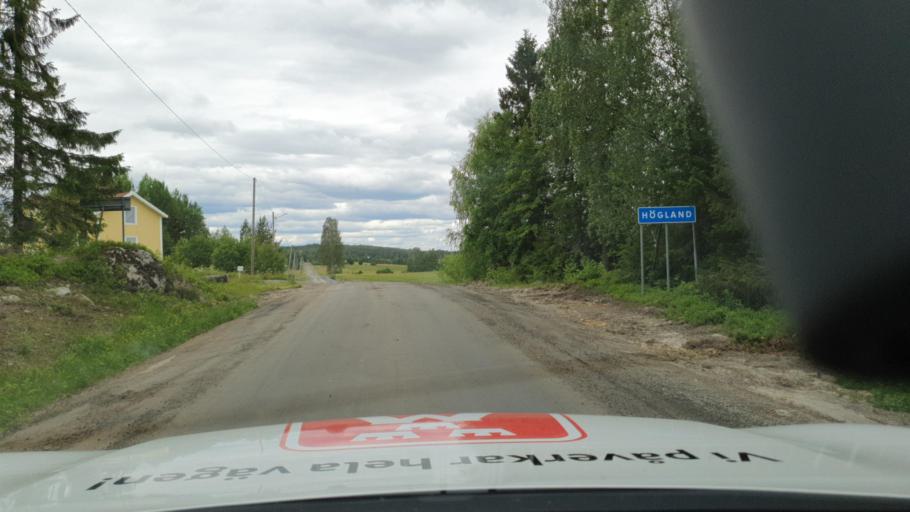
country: SE
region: Vaesterbotten
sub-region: Nordmalings Kommun
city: Nordmaling
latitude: 63.7039
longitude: 19.4408
